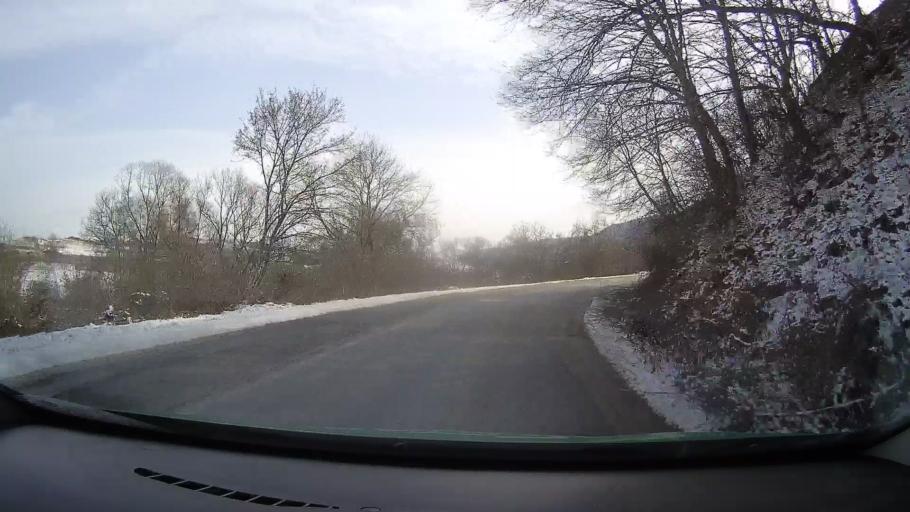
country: RO
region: Mures
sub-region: Comuna Apold
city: Saes
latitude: 46.1699
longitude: 24.7578
